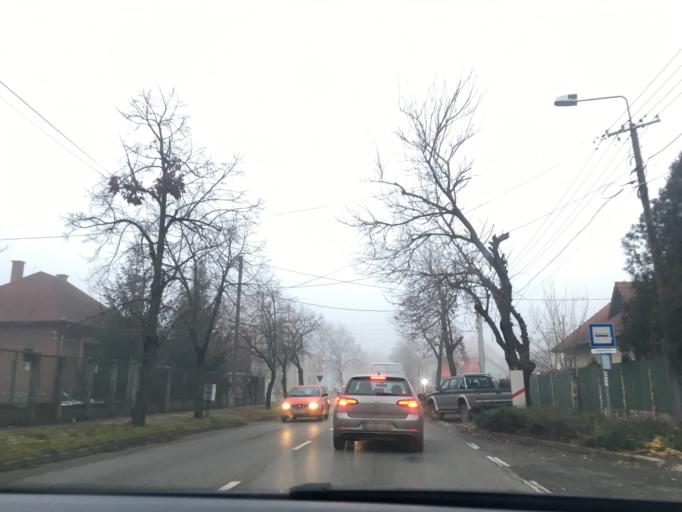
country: HU
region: Hajdu-Bihar
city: Debrecen
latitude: 47.5350
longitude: 21.6478
